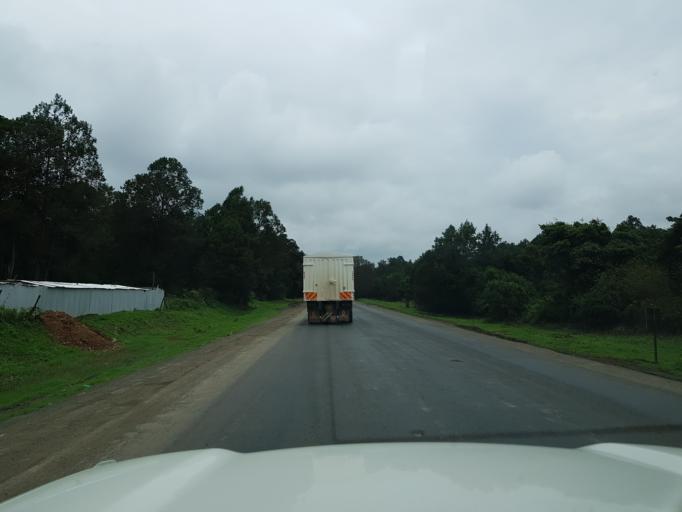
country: KE
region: Kiambu
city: Limuru
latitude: -1.0927
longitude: 36.6065
